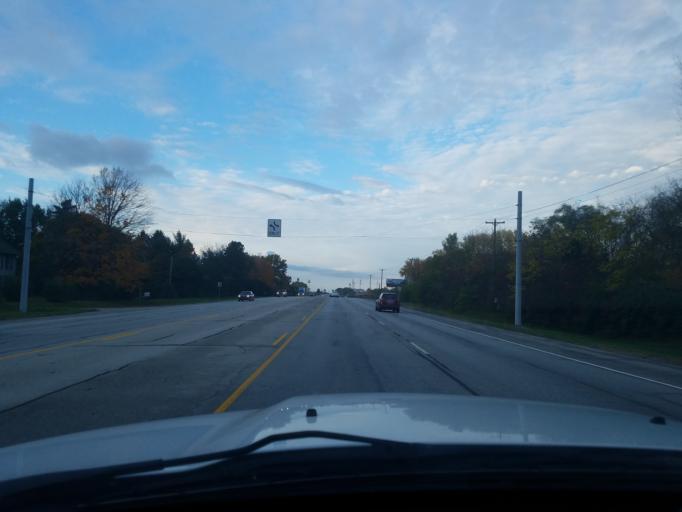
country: US
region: Indiana
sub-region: Shelby County
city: Shelbyville
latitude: 39.5411
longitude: -85.7753
